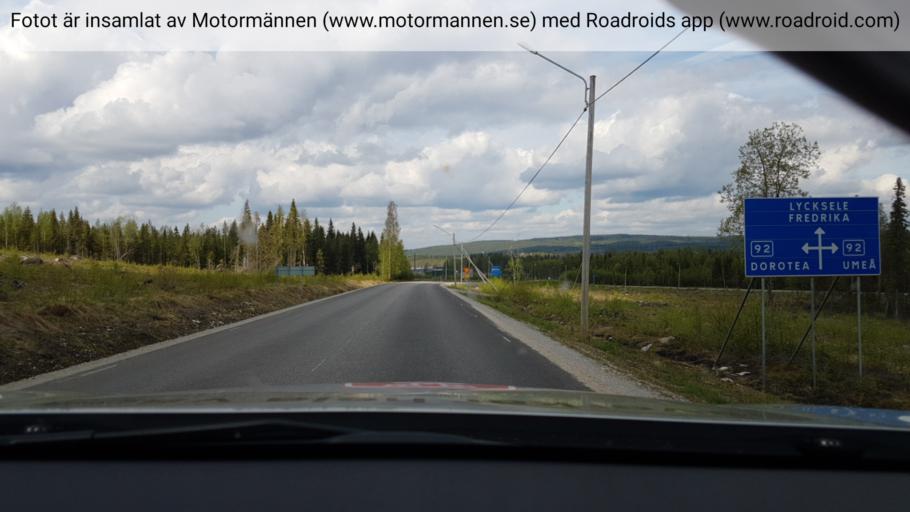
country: SE
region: Vaesterbotten
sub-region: Lycksele Kommun
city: Lycksele
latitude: 64.0667
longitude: 18.3986
